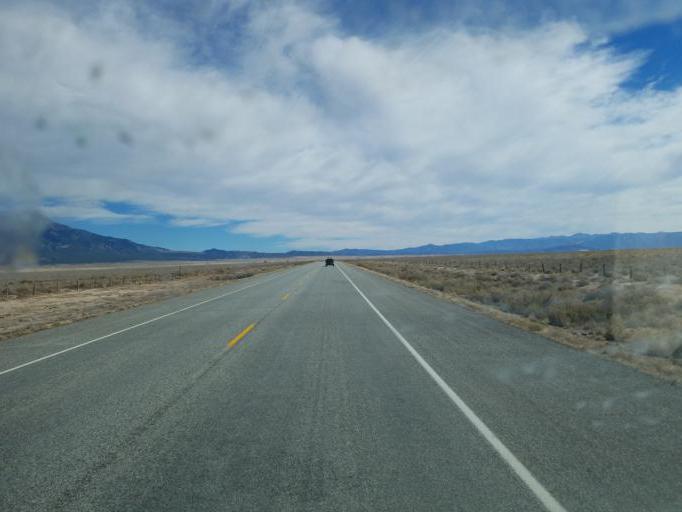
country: US
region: Colorado
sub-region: Alamosa County
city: Alamosa East
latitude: 37.4748
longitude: -105.6644
